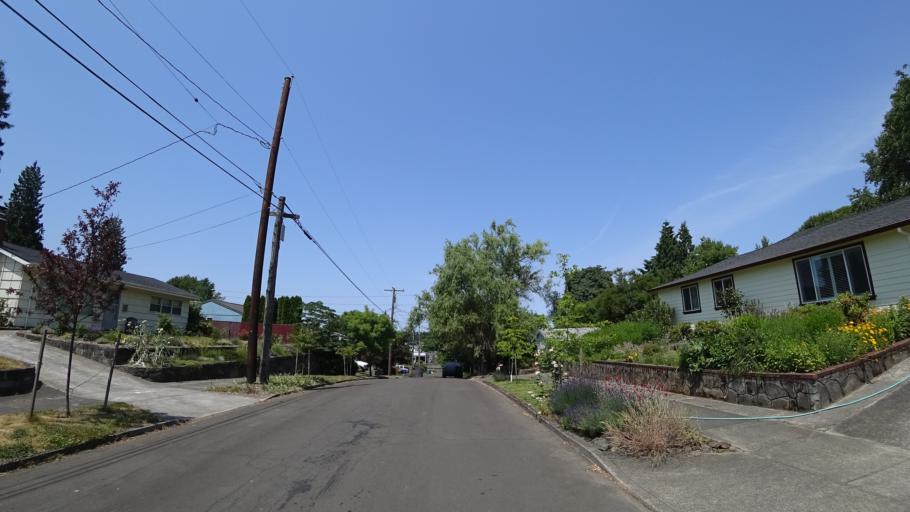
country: US
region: Washington
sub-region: Clark County
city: Vancouver
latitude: 45.5863
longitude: -122.6941
